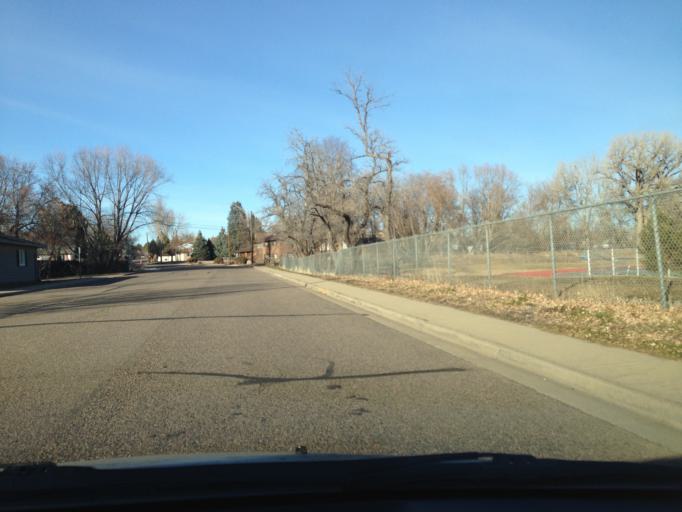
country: US
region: Colorado
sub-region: Boulder County
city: Louisville
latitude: 39.9843
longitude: -105.1345
